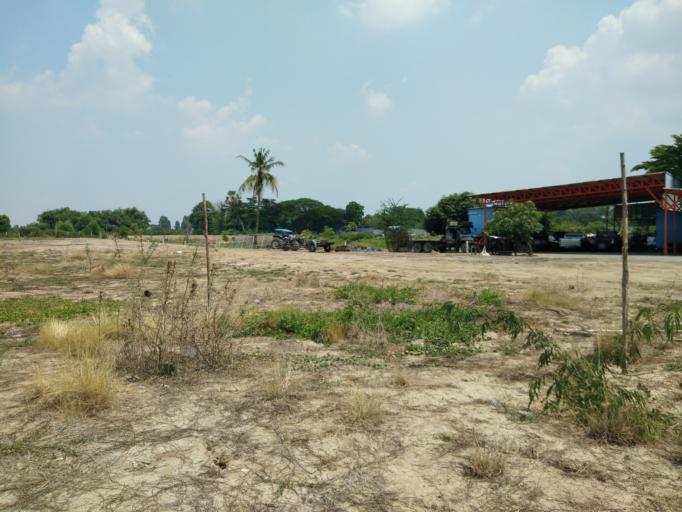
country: TH
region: Suphan Buri
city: Bang Pla Ma
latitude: 14.2865
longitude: 100.1321
